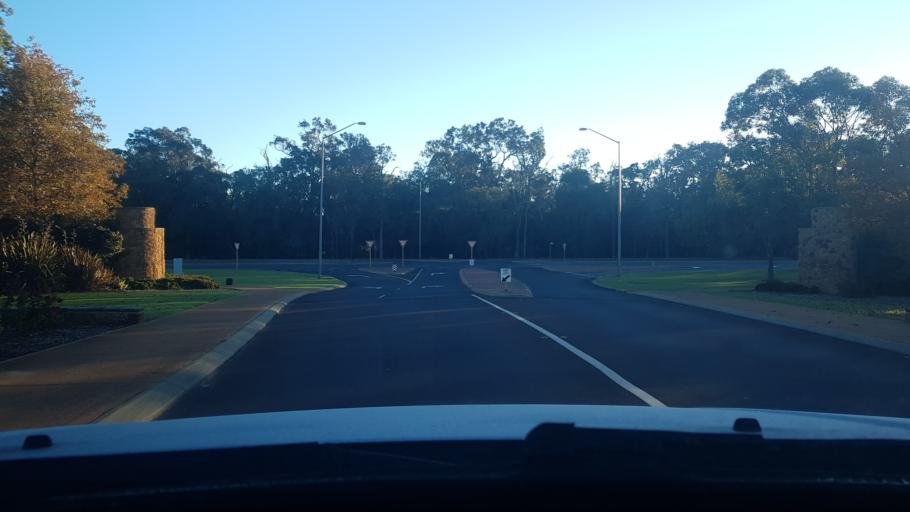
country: AU
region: Western Australia
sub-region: Busselton
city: Vasse
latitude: -33.6766
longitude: 115.2593
